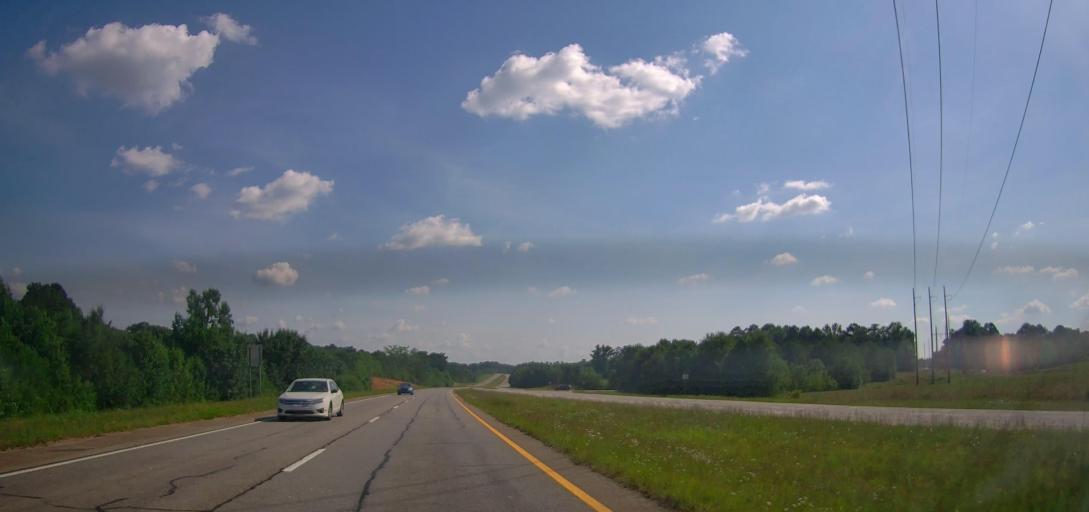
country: US
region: Georgia
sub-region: Henry County
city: Hampton
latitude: 33.3874
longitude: -84.2589
